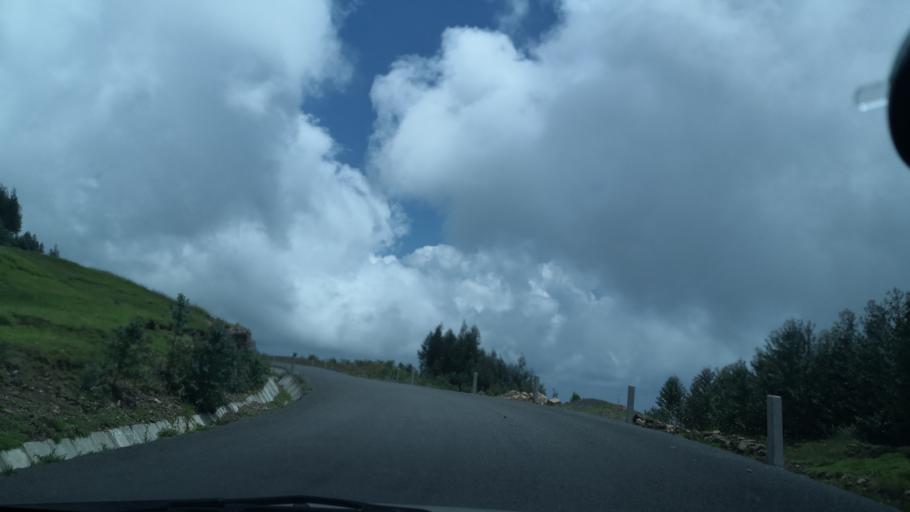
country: ET
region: Amhara
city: Kemise
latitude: 10.3605
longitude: 39.8293
